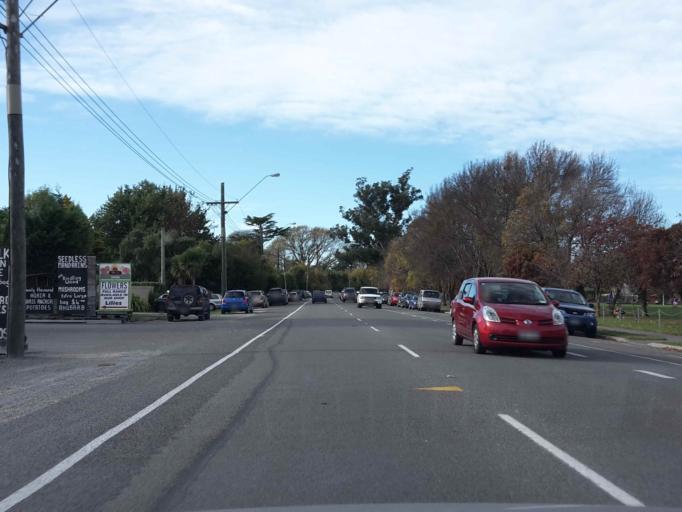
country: NZ
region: Canterbury
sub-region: Christchurch City
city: Christchurch
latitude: -43.4808
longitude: 172.5692
